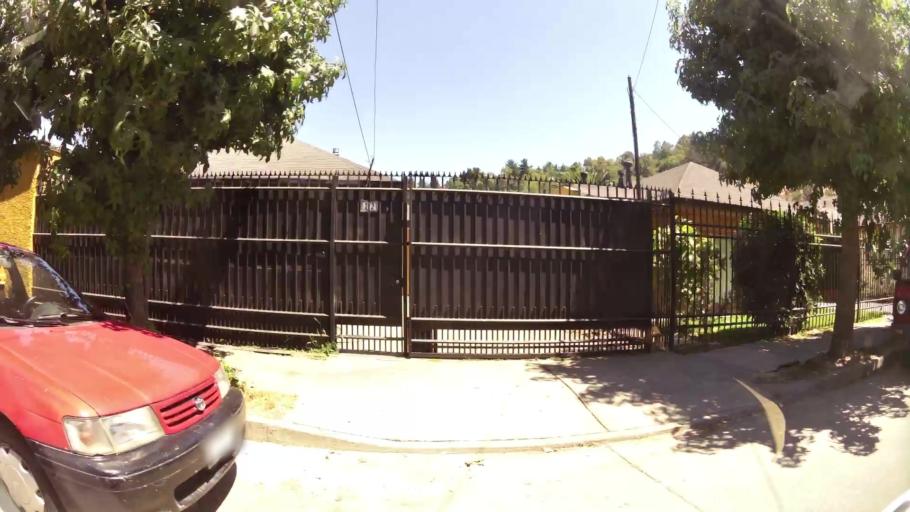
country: CL
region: Maule
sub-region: Provincia de Curico
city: Curico
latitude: -34.9828
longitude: -71.2293
